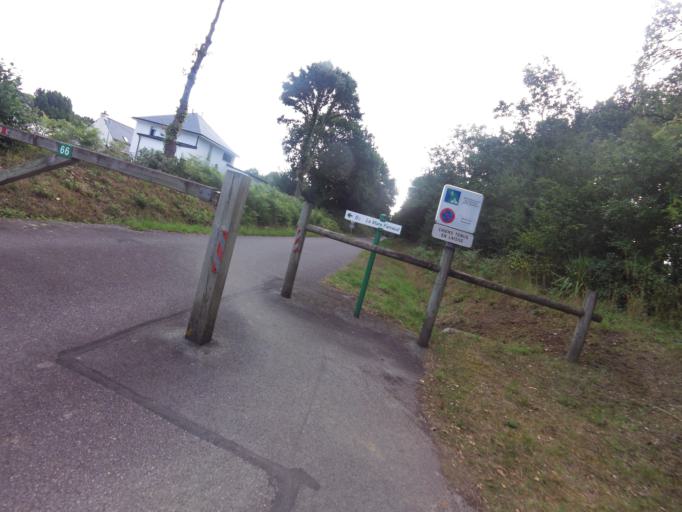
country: FR
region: Brittany
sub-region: Departement du Morbihan
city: Ploermel
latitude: 47.9229
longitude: -2.4188
